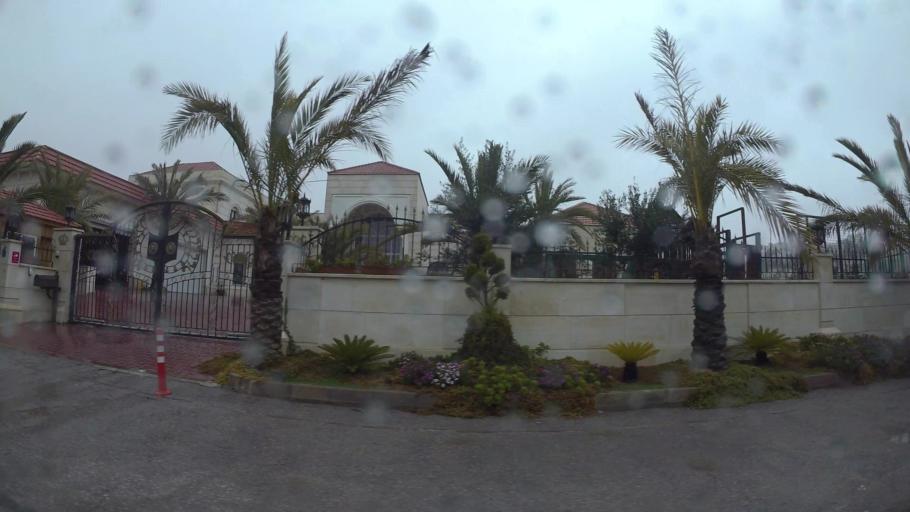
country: JO
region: Amman
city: Wadi as Sir
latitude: 31.9939
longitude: 35.8269
